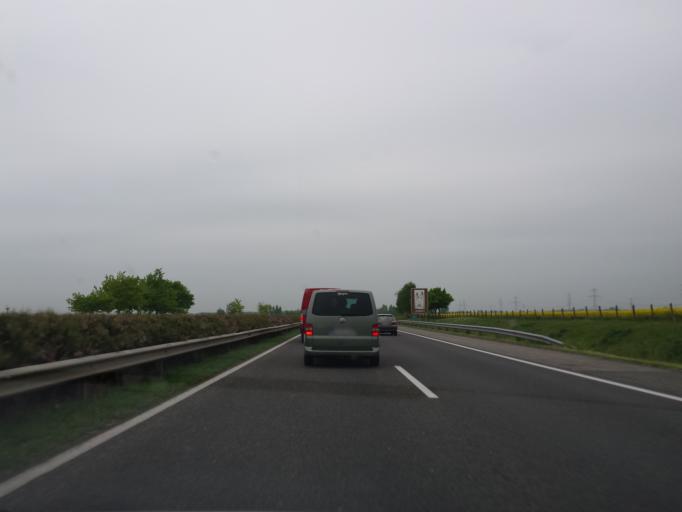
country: HU
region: Gyor-Moson-Sopron
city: Mosonszentmiklos
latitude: 47.7306
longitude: 17.4457
